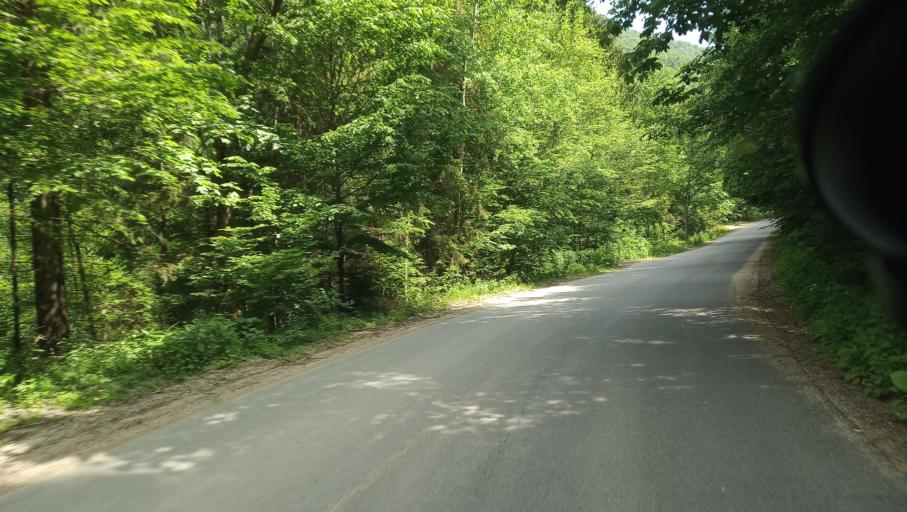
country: RO
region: Cluj
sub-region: Comuna Maguri-Racatau
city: Maguri-Racatau
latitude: 46.7089
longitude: 23.2388
